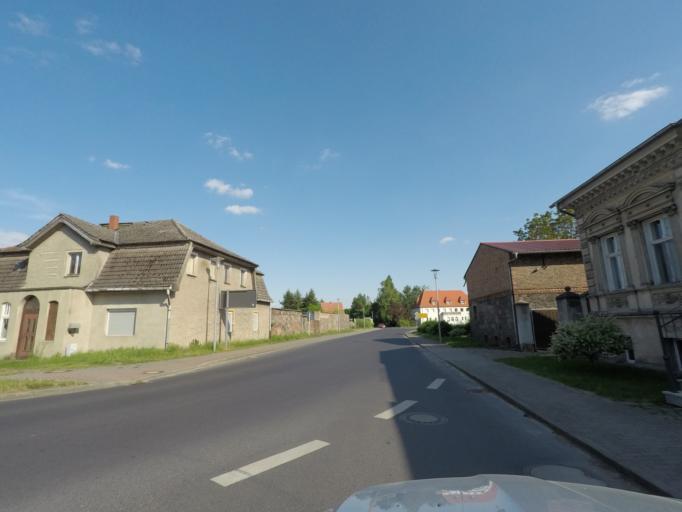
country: DE
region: Brandenburg
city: Werftpfuhl
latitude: 52.7373
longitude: 13.8383
